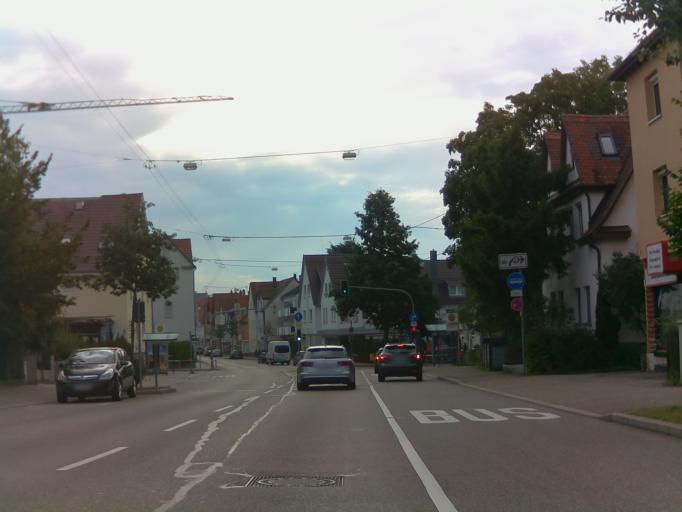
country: DE
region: Baden-Wuerttemberg
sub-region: Regierungsbezirk Stuttgart
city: Steinenbronn
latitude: 48.7302
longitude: 9.1016
